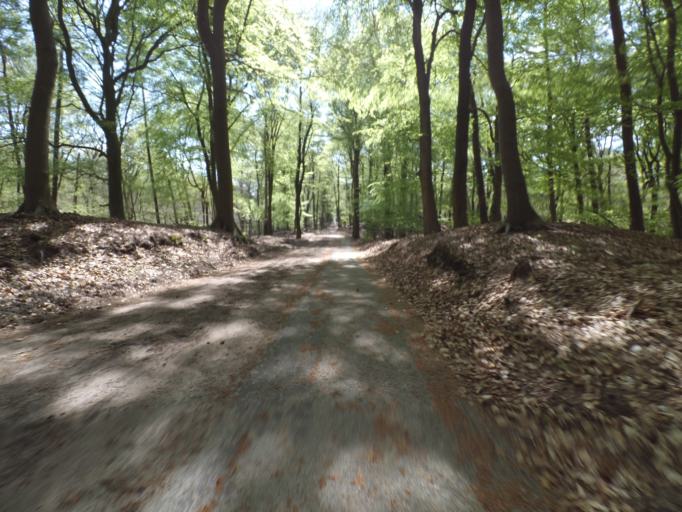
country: NL
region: Gelderland
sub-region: Gemeente Ermelo
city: Ermelo
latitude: 52.3222
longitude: 5.7026
